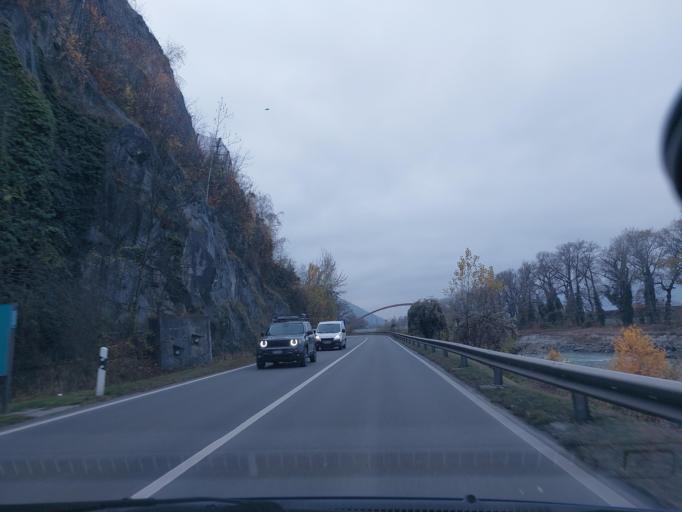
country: CH
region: Valais
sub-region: Sion District
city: Sitten
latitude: 46.2183
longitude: 7.3551
